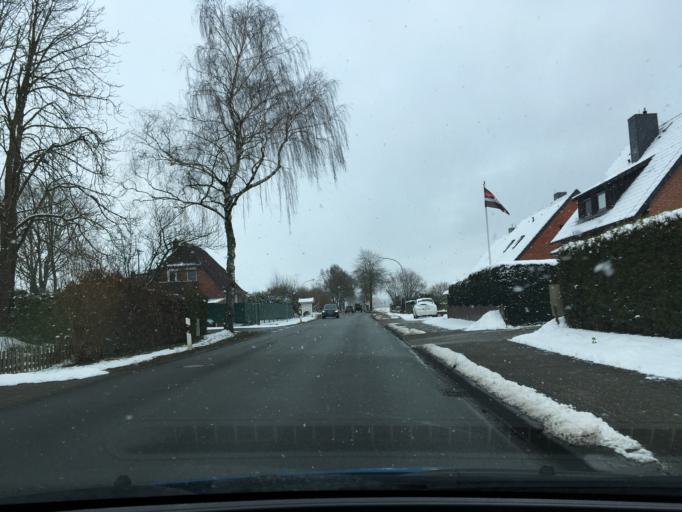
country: DE
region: Lower Saxony
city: Winsen
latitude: 53.3288
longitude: 10.2051
